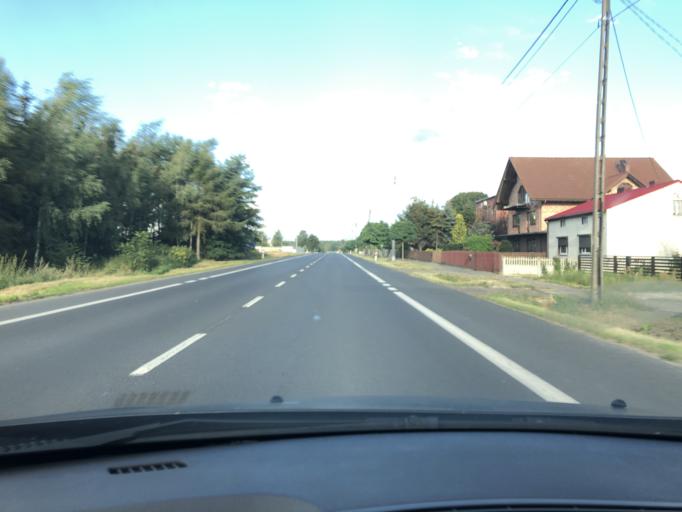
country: PL
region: Lodz Voivodeship
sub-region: Powiat wieruszowski
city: Galewice
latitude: 51.3040
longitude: 18.2477
